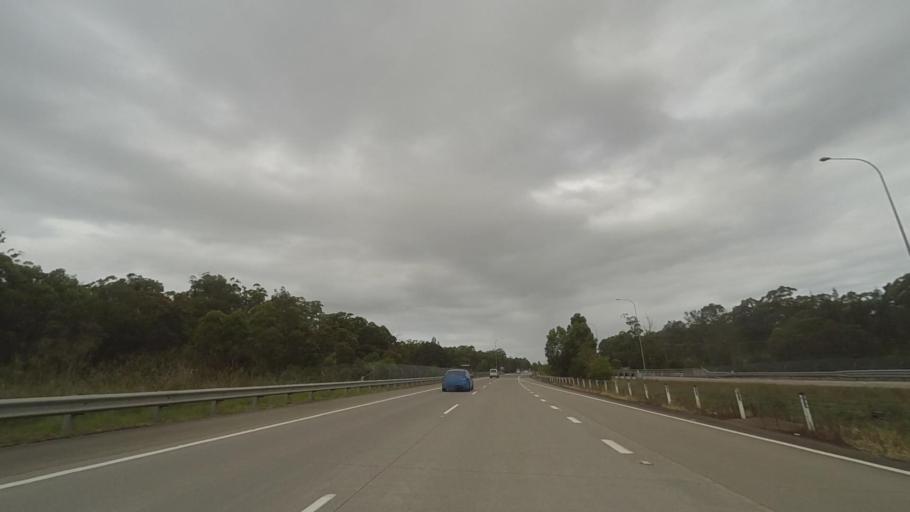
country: AU
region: New South Wales
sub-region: Port Stephens Shire
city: Port Stephens
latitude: -32.6115
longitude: 152.0843
